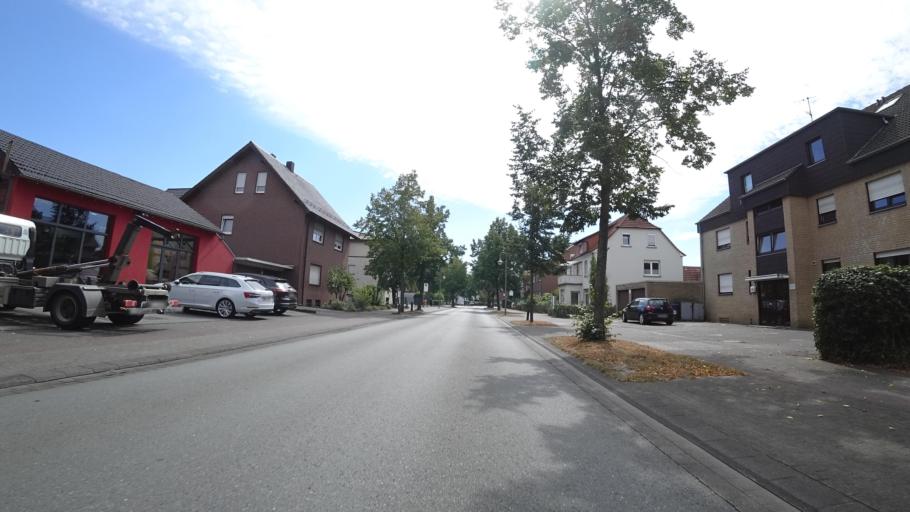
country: DE
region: North Rhine-Westphalia
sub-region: Regierungsbezirk Detmold
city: Steinhagen
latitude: 51.9518
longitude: 8.4009
